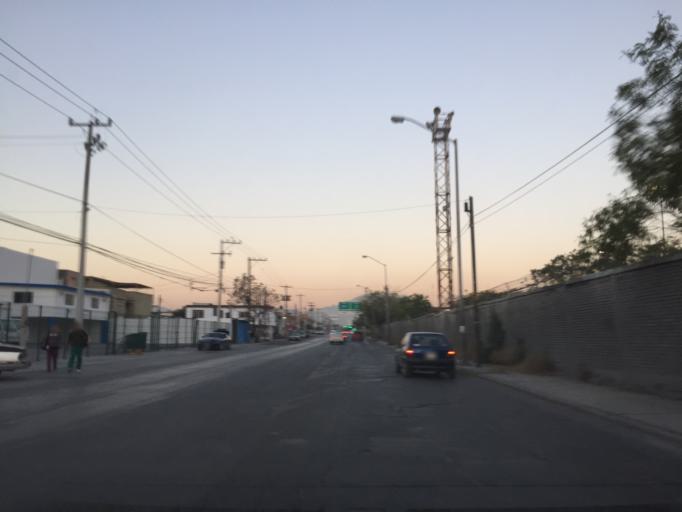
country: MX
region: Nuevo Leon
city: Guadalupe
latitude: 25.6953
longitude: -100.2260
